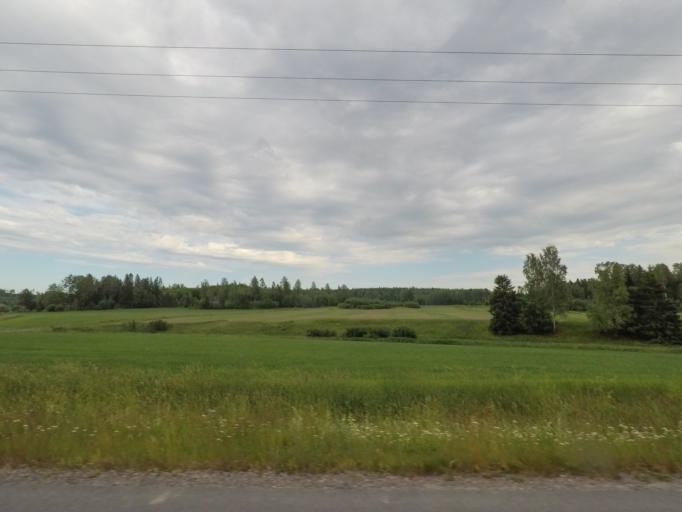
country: FI
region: Uusimaa
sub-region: Helsinki
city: Maentsaelae
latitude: 60.6900
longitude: 25.3753
